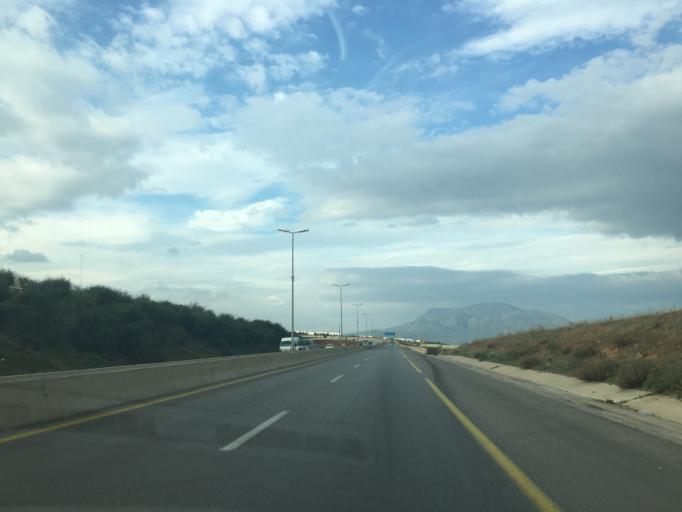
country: DZ
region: Tipaza
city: Tipasa
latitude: 36.5764
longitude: 2.5107
